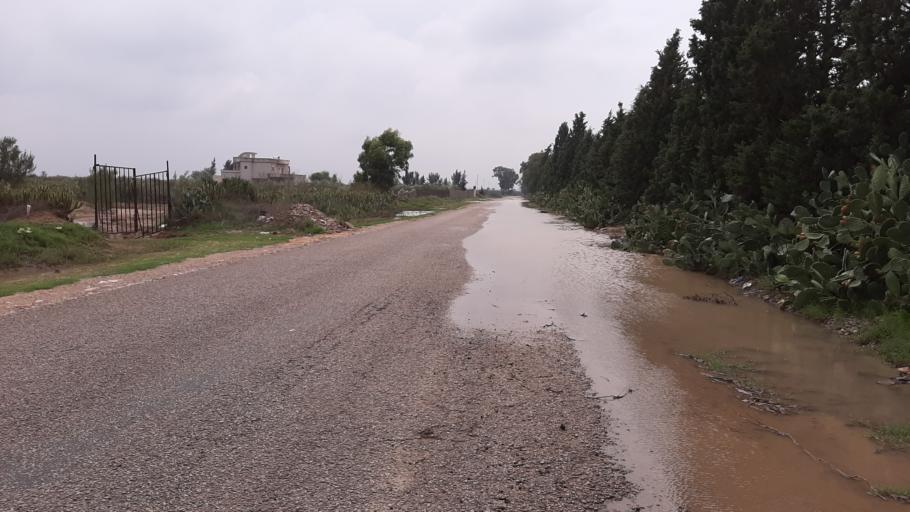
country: TN
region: Al Munastir
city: Sidi Bin Nur
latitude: 35.4548
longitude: 10.9043
